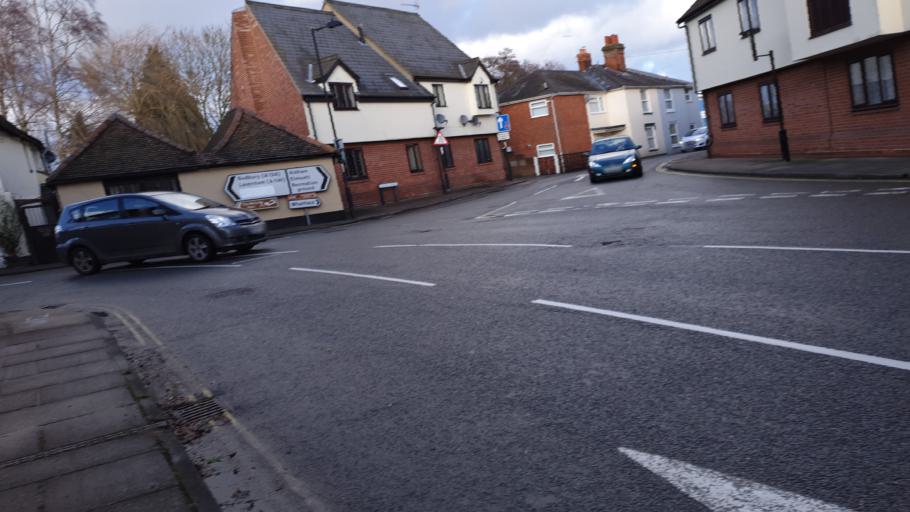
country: GB
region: England
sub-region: Suffolk
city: Hadleigh
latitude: 52.0468
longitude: 0.9517
